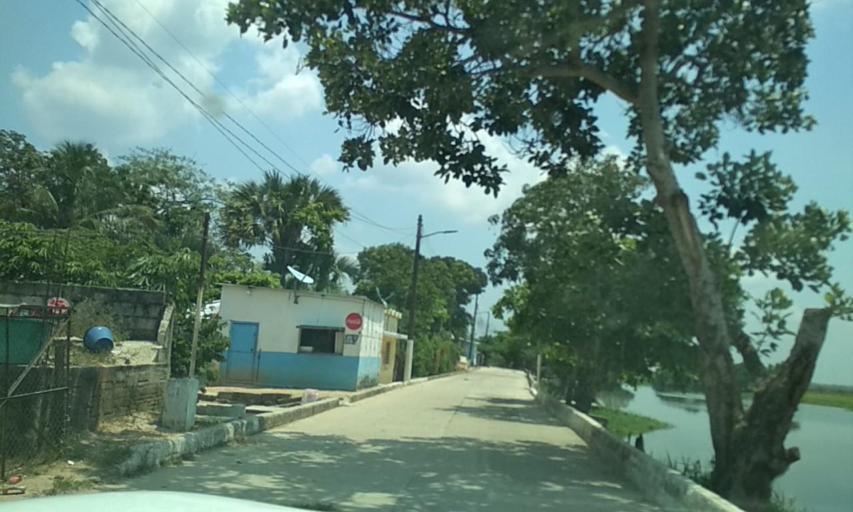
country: MX
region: Veracruz
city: Las Choapas
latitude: 17.9123
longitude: -94.0868
